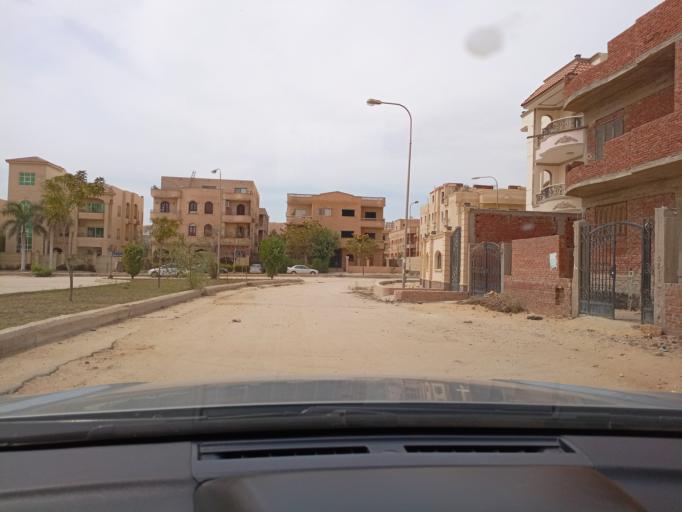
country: EG
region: Muhafazat al Qalyubiyah
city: Al Khankah
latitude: 30.2358
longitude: 31.4936
